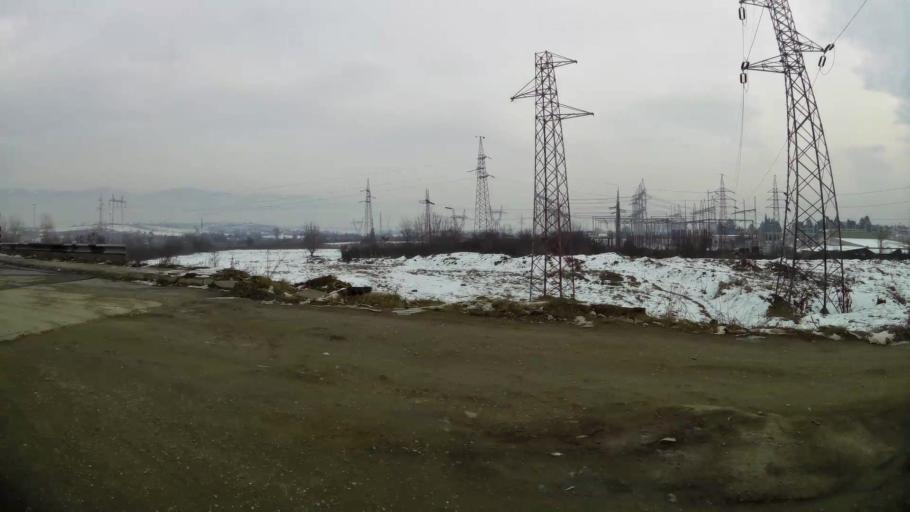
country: MK
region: Butel
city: Butel
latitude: 42.0395
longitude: 21.4546
